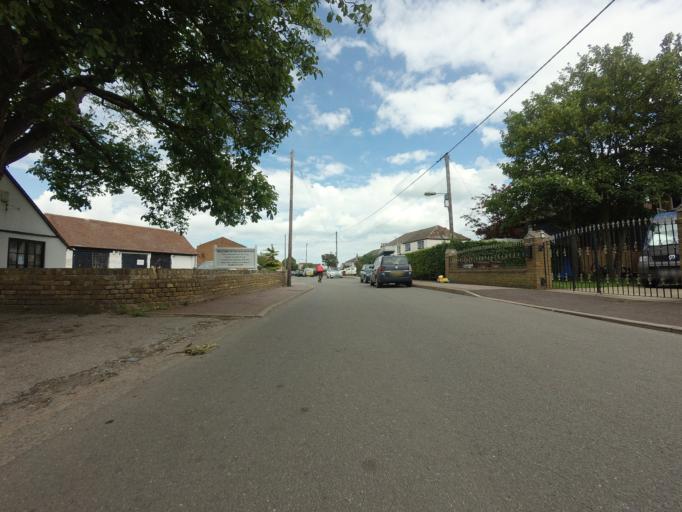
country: GB
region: England
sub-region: Kent
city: Sheerness
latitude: 51.4567
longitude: 0.7136
